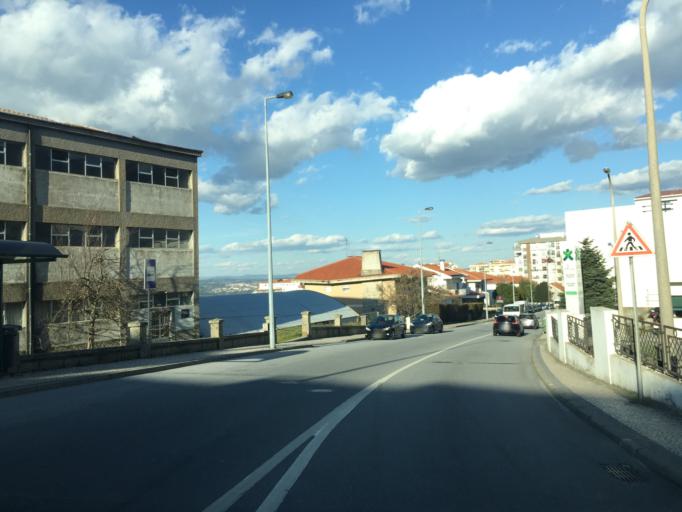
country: PT
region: Guarda
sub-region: Seia
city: Seia
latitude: 40.4145
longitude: -7.7106
